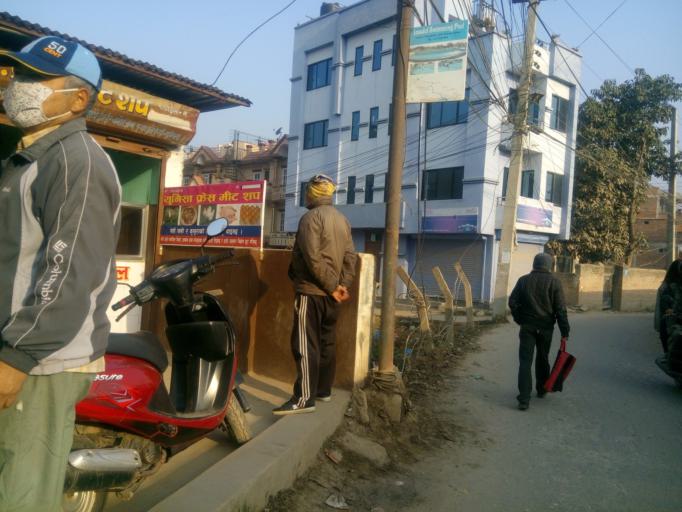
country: NP
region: Central Region
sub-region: Bagmati Zone
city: Patan
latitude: 27.6616
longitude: 85.3366
